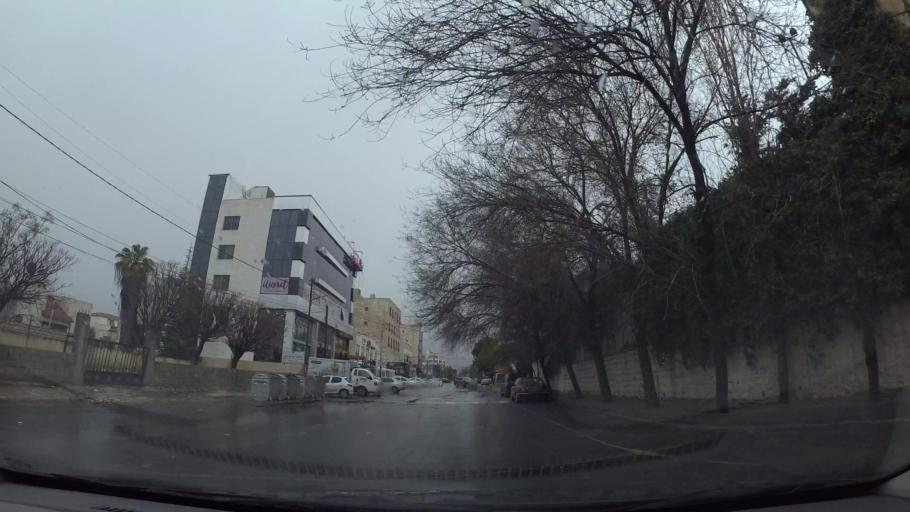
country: JO
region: Amman
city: Wadi as Sir
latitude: 31.9654
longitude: 35.8454
